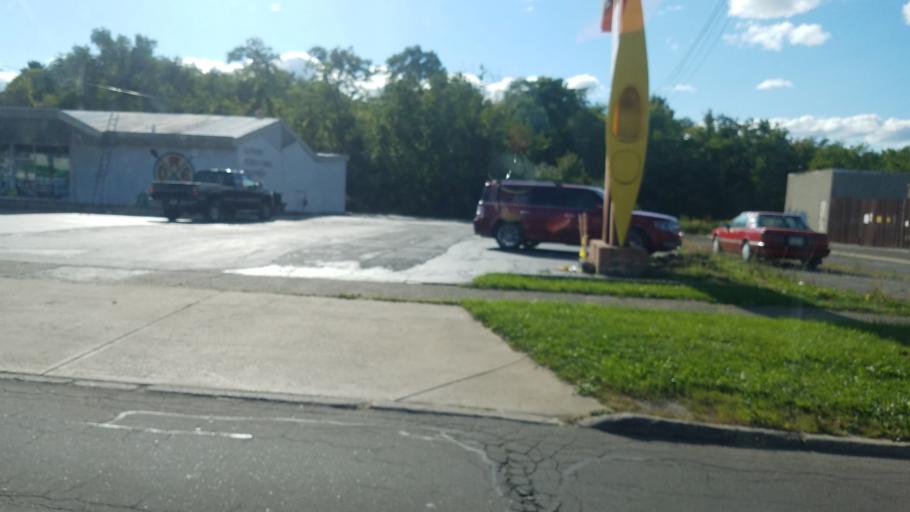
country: US
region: Ohio
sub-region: Mahoning County
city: Boardman
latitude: 41.0453
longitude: -80.6628
